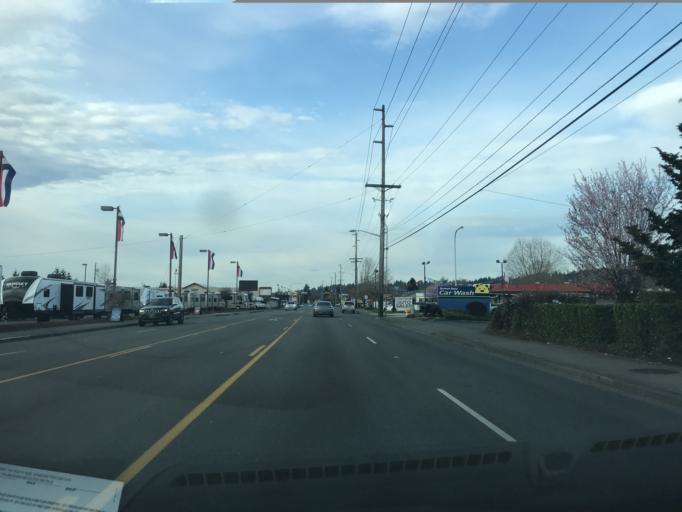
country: US
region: Washington
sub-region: King County
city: Auburn
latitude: 47.3420
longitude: -122.2222
